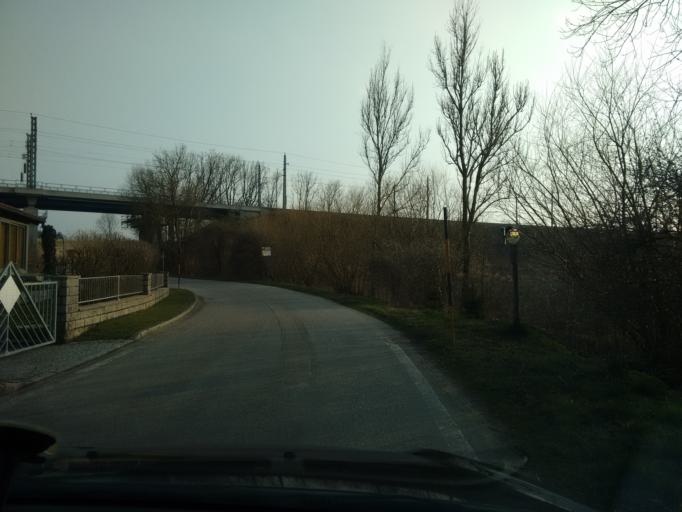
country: AT
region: Upper Austria
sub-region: Politischer Bezirk Grieskirchen
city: Bad Schallerbach
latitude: 48.2158
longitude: 13.9565
